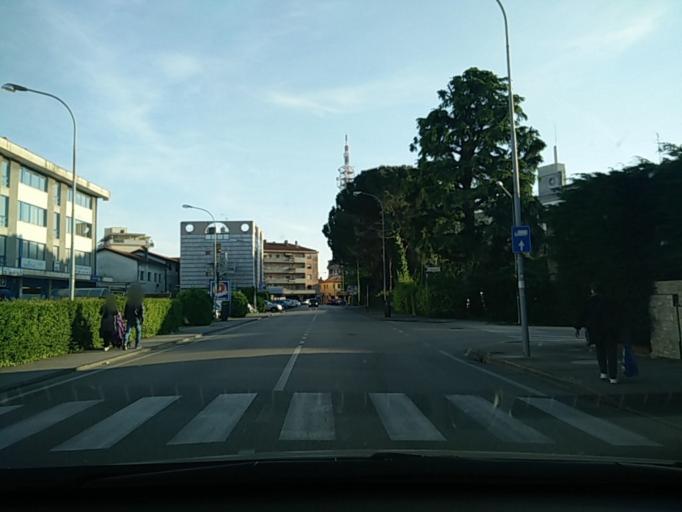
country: IT
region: Veneto
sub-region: Provincia di Venezia
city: San Dona di Piave
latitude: 45.6321
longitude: 12.5764
